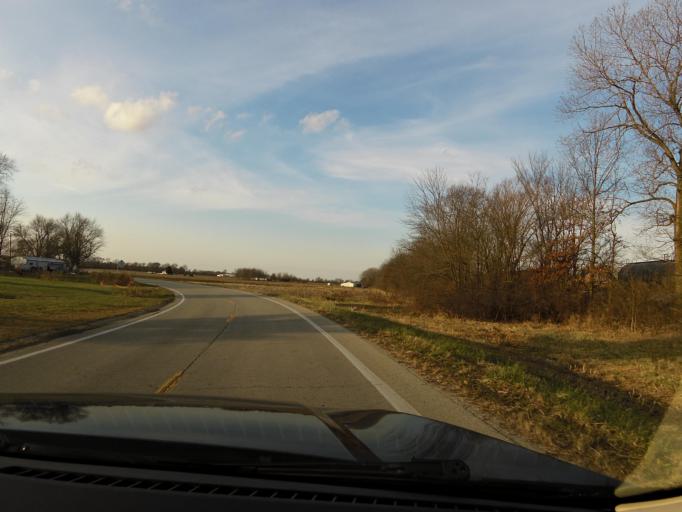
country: US
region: Illinois
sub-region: Fayette County
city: Vandalia
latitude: 38.9430
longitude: -89.1701
